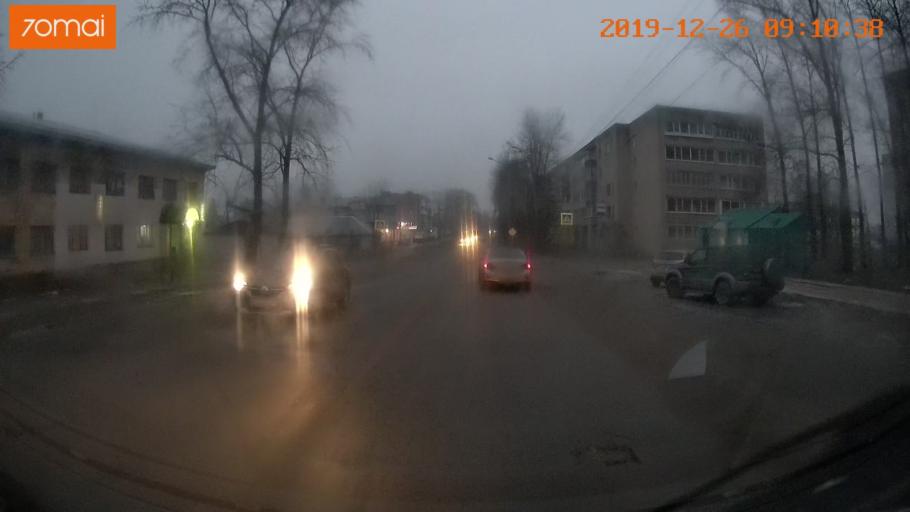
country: RU
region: Vologda
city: Gryazovets
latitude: 58.8721
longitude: 40.2525
